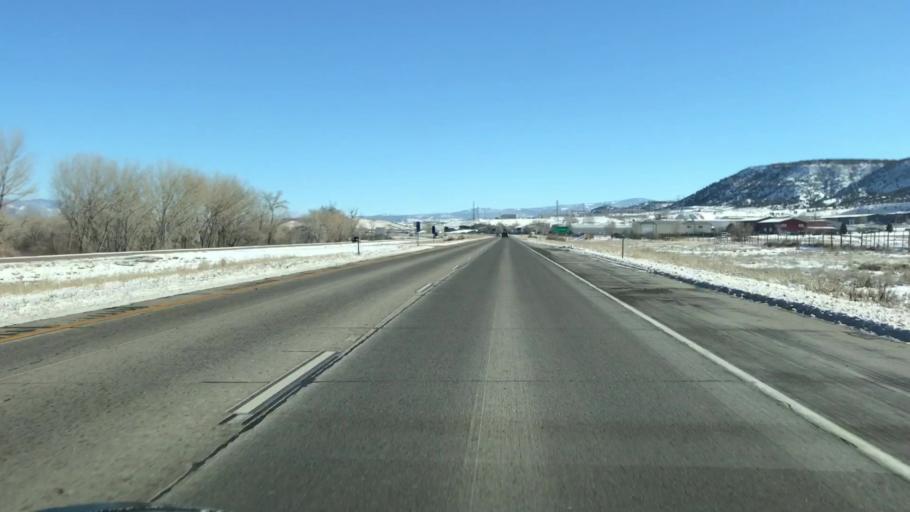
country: US
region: Colorado
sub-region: Garfield County
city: Rifle
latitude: 39.5251
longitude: -107.7618
